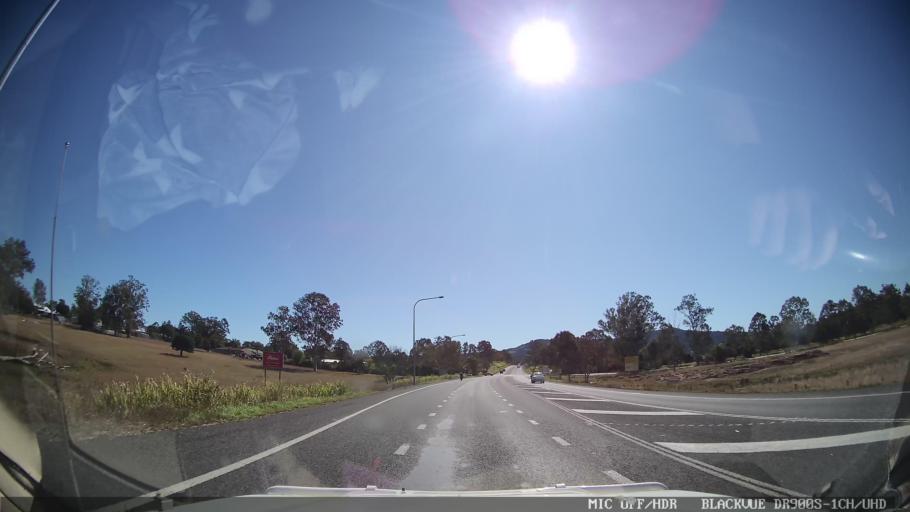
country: AU
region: Queensland
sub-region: Gympie Regional Council
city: Gympie
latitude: -25.9966
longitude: 152.5665
